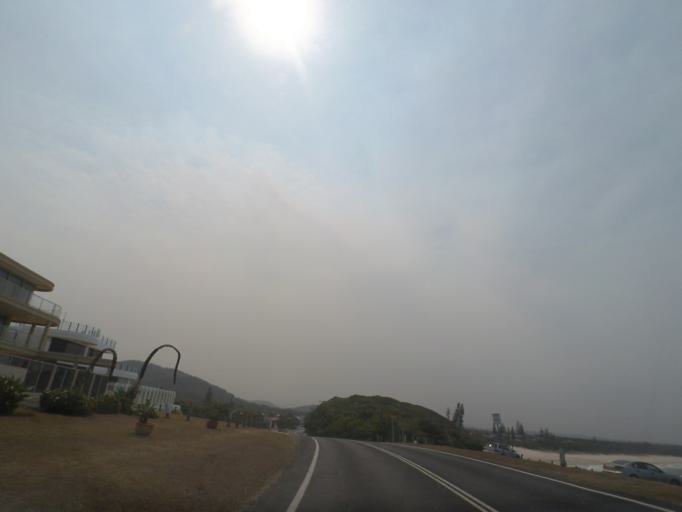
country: AU
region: New South Wales
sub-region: Tweed
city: Casuarina
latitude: -28.3349
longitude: 153.5738
